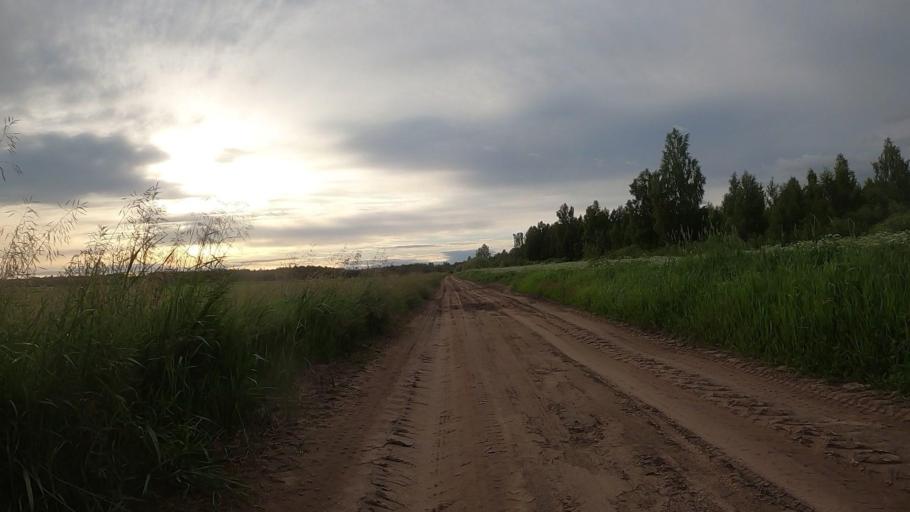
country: LV
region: Olaine
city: Olaine
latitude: 56.8268
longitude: 23.9655
